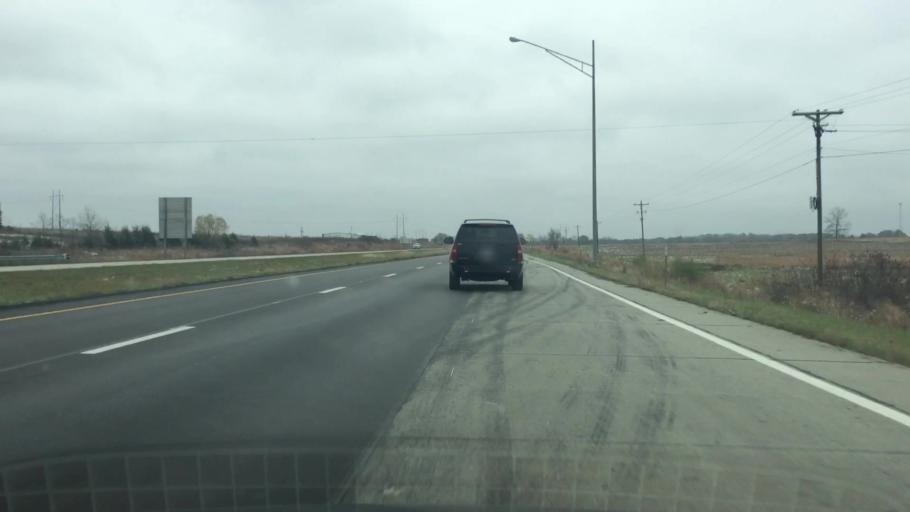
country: US
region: Missouri
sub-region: Saint Clair County
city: Osceola
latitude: 38.0370
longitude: -93.6799
